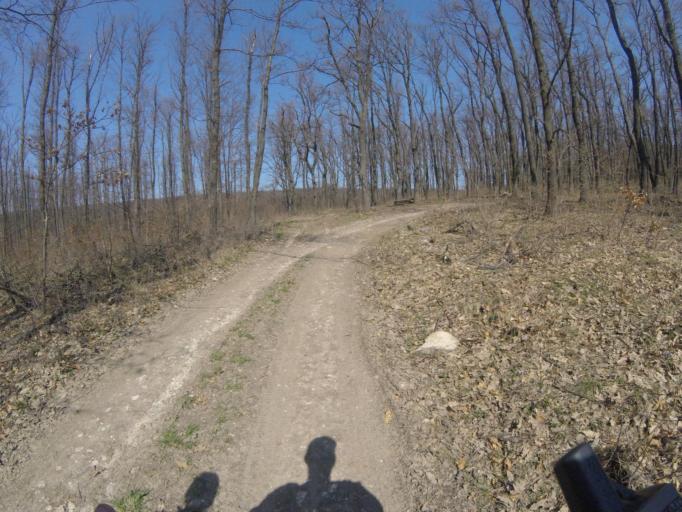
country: HU
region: Pest
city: Budakeszi
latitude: 47.5488
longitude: 18.8910
